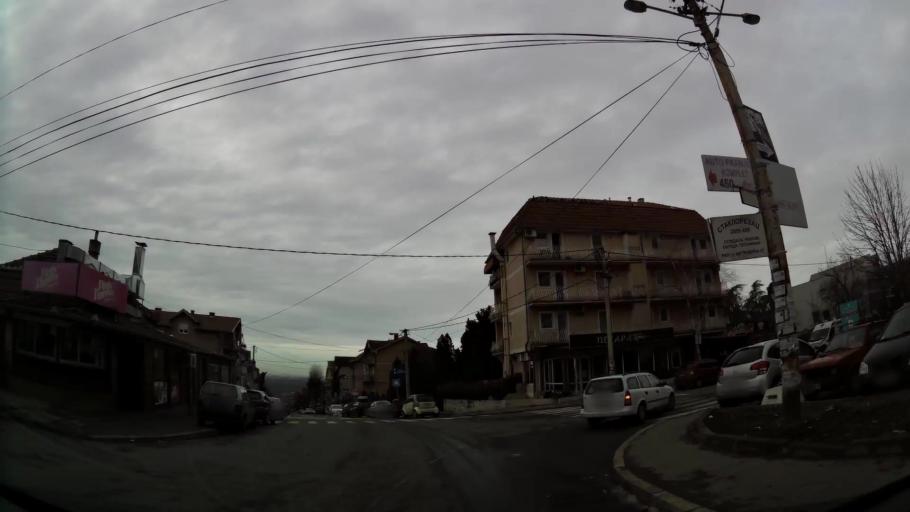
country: RS
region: Central Serbia
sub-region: Belgrade
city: Cukarica
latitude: 44.7594
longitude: 20.4125
